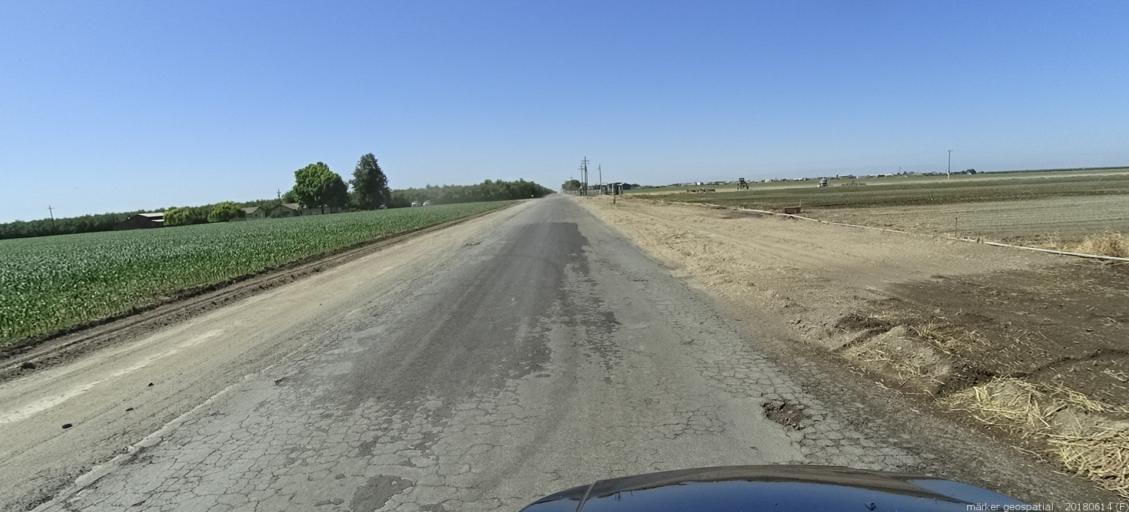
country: US
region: California
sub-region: Madera County
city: Fairmead
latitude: 36.9471
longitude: -120.2380
